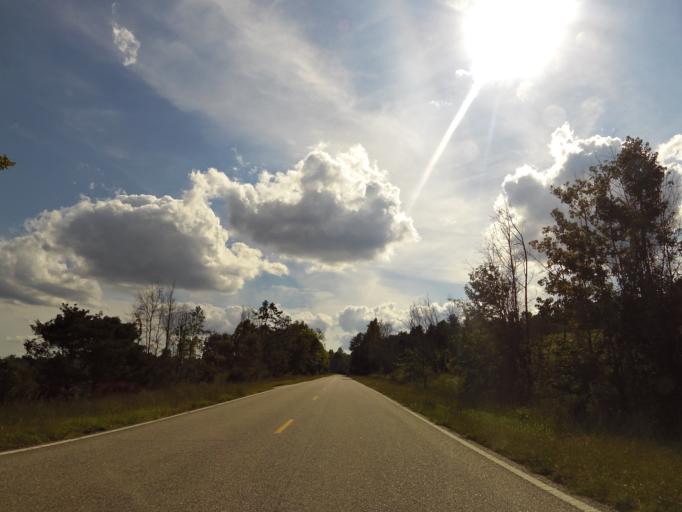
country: US
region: Alabama
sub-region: Dallas County
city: Selmont-West Selmont
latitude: 32.1715
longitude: -87.0524
